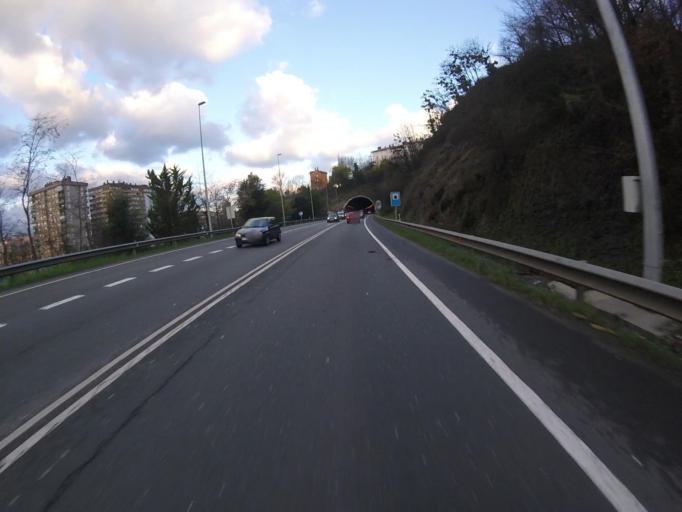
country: ES
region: Basque Country
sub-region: Provincia de Guipuzcoa
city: Lezo
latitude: 43.3152
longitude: -1.8964
